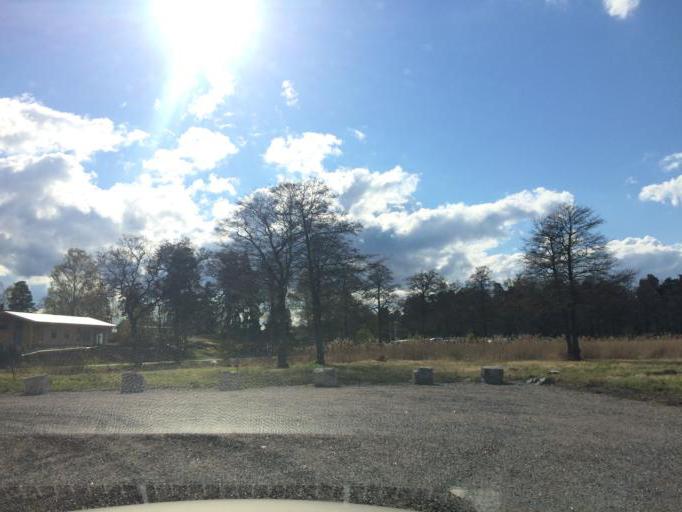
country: SE
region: Soedermanland
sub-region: Eskilstuna Kommun
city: Eskilstuna
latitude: 59.4463
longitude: 16.6202
